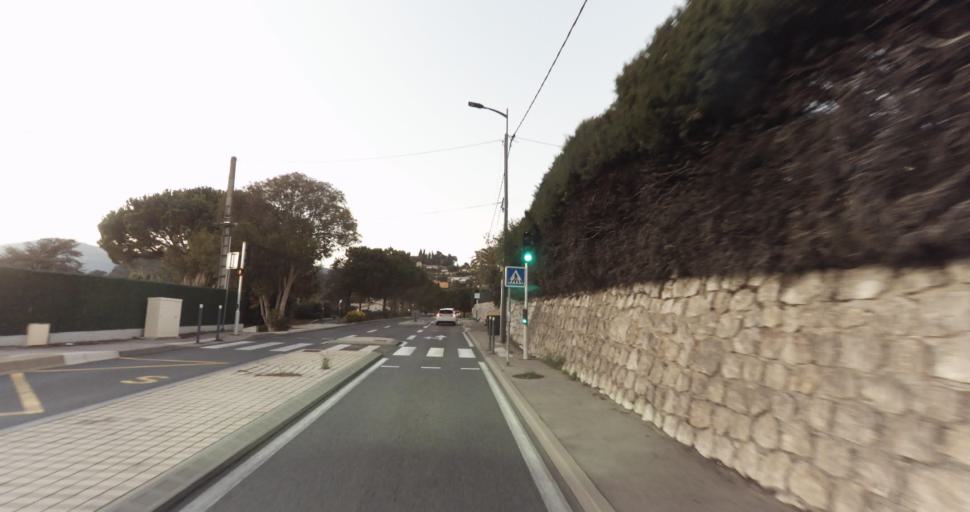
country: FR
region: Provence-Alpes-Cote d'Azur
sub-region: Departement des Alpes-Maritimes
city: Saint-Paul-de-Vence
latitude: 43.7105
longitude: 7.1262
